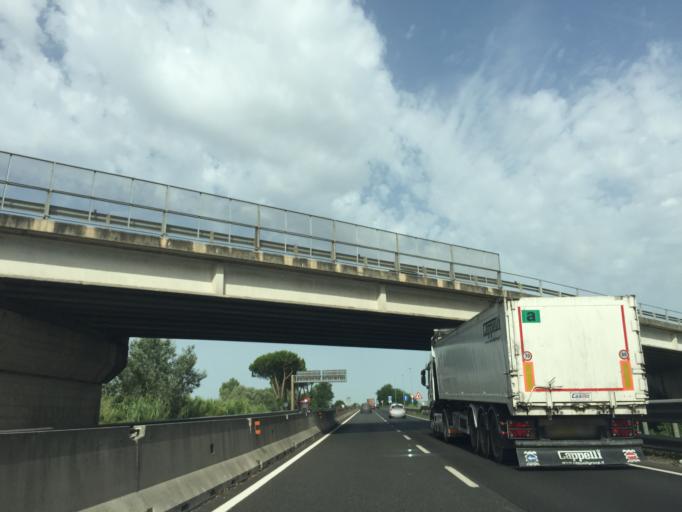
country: IT
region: Tuscany
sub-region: Province of Pisa
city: Montopoli
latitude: 43.6716
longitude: 10.7296
